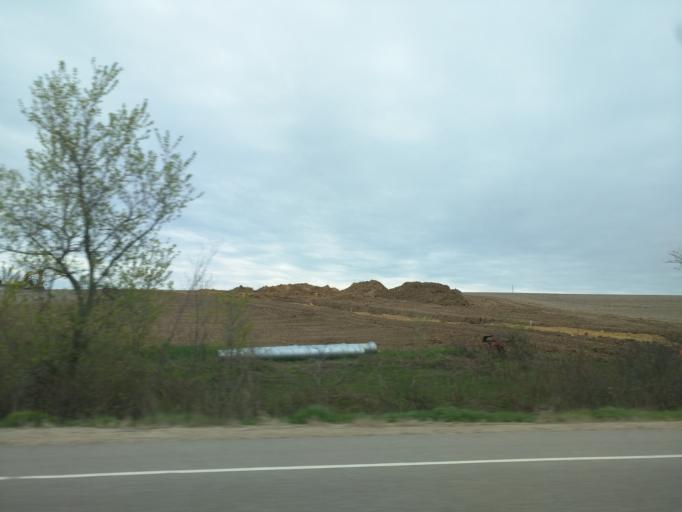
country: US
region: Minnesota
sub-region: Goodhue County
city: Red Wing
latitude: 44.5872
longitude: -92.3902
